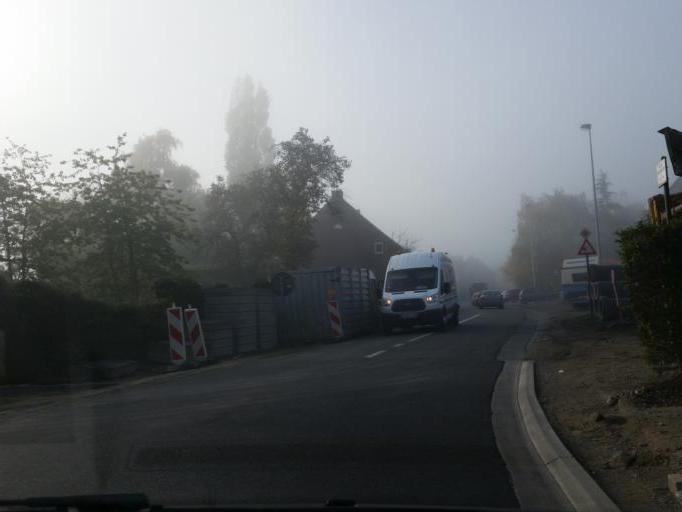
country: BE
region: Flanders
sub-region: Provincie Vlaams-Brabant
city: Opwijk
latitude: 50.9568
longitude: 4.1442
